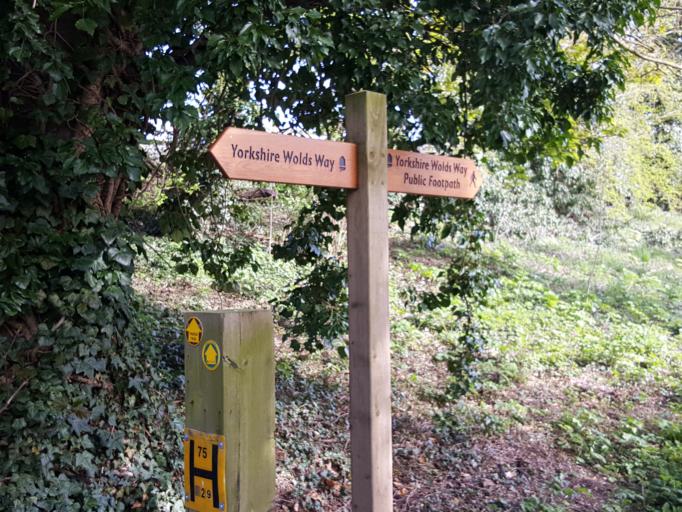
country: GB
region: England
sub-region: East Riding of Yorkshire
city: Welton
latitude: 53.7367
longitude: -0.5450
